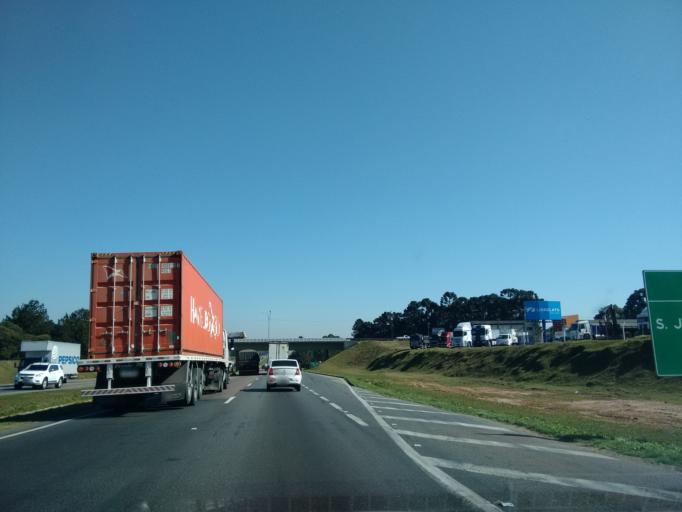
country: BR
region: Parana
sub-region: Sao Jose Dos Pinhais
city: Sao Jose dos Pinhais
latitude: -25.5701
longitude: -49.2176
